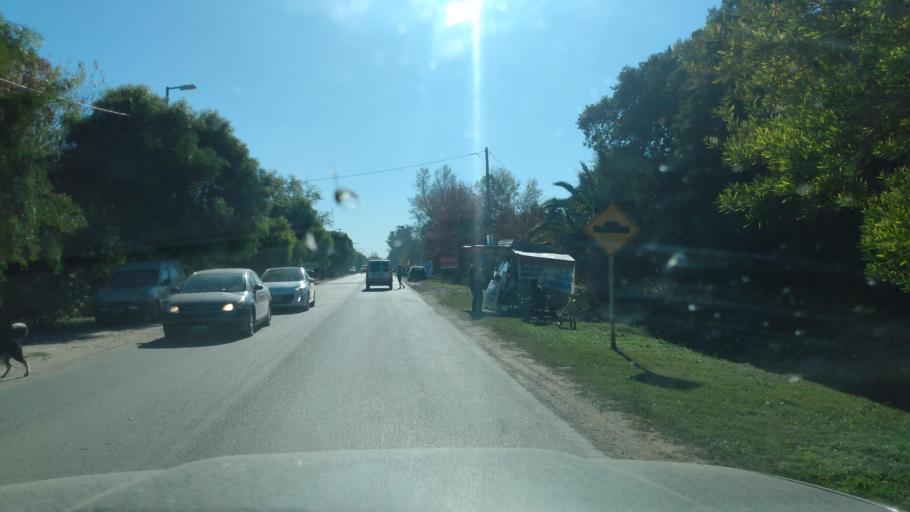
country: AR
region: Buenos Aires
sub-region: Partido de Lujan
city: Lujan
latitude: -34.4882
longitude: -59.2130
